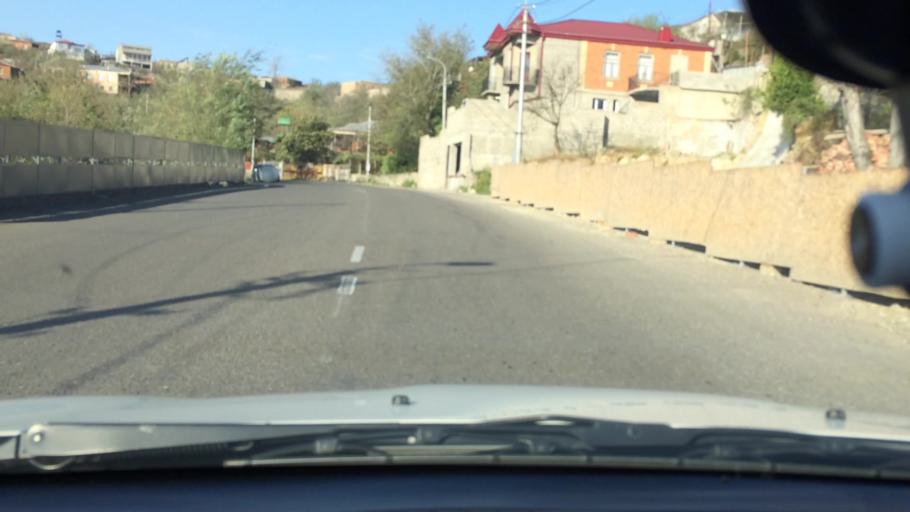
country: GE
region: Imereti
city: Kutaisi
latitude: 42.2654
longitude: 42.7240
